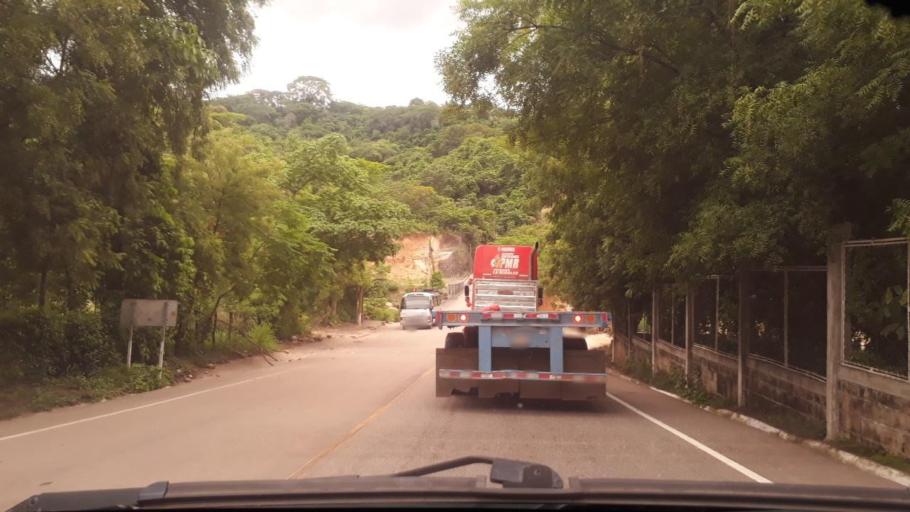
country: GT
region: Chiquimula
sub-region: Municipio de Camotan
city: Camotan
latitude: 14.8503
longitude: -89.3395
